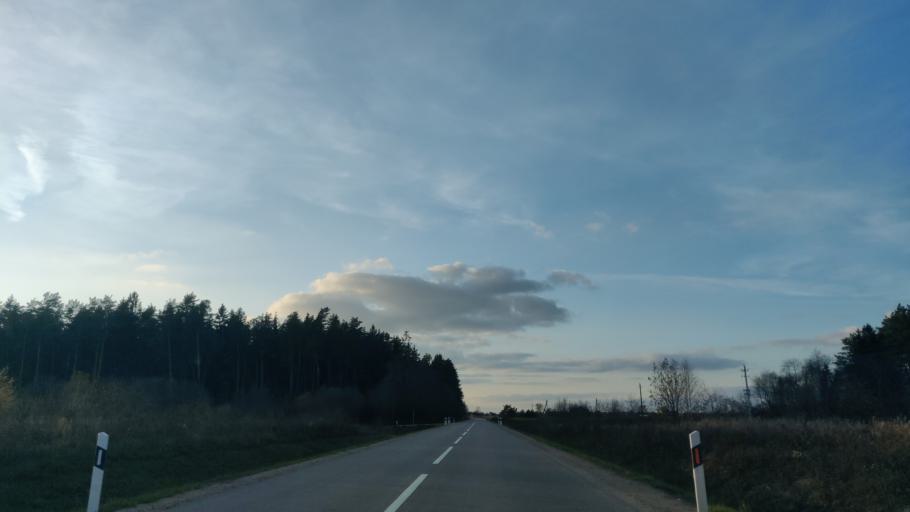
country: LT
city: Lentvaris
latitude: 54.5980
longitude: 25.0277
